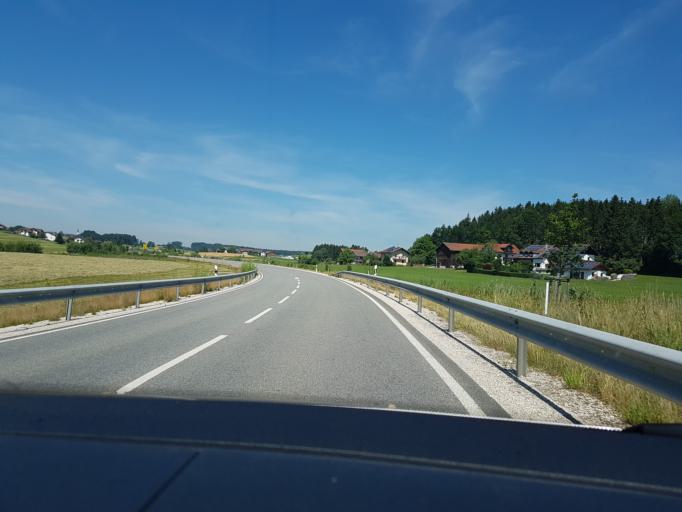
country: DE
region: Bavaria
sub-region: Upper Bavaria
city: Ainring
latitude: 47.8350
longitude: 12.9221
